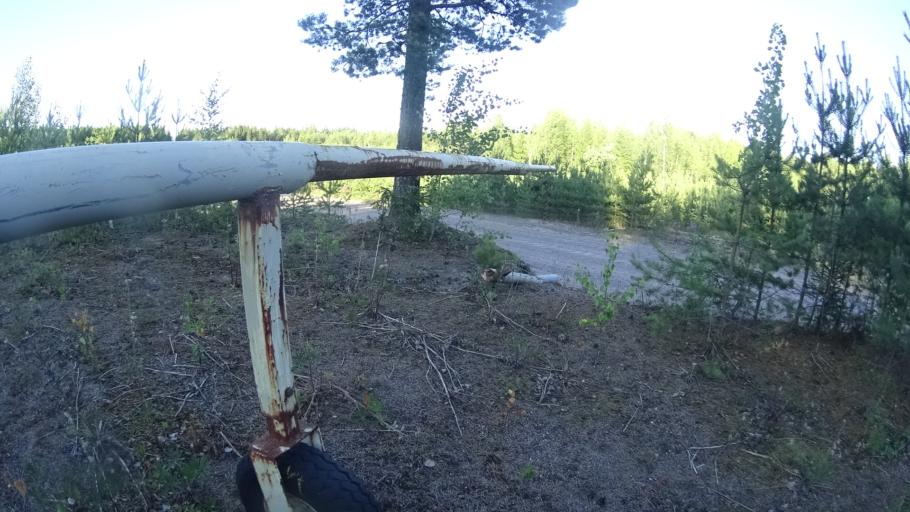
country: FI
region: Uusimaa
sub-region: Helsinki
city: Karkkila
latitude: 60.5961
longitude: 24.1230
